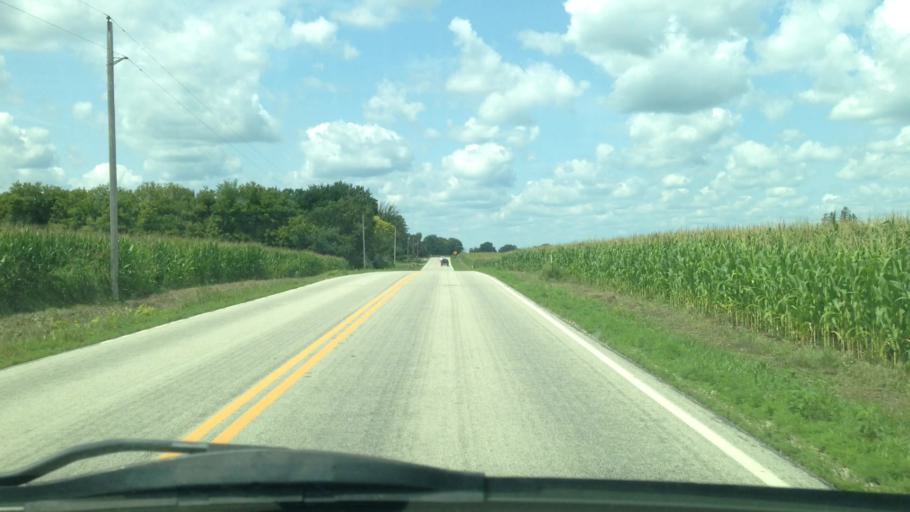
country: US
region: Minnesota
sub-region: Olmsted County
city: Rochester
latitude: 43.9532
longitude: -92.5116
